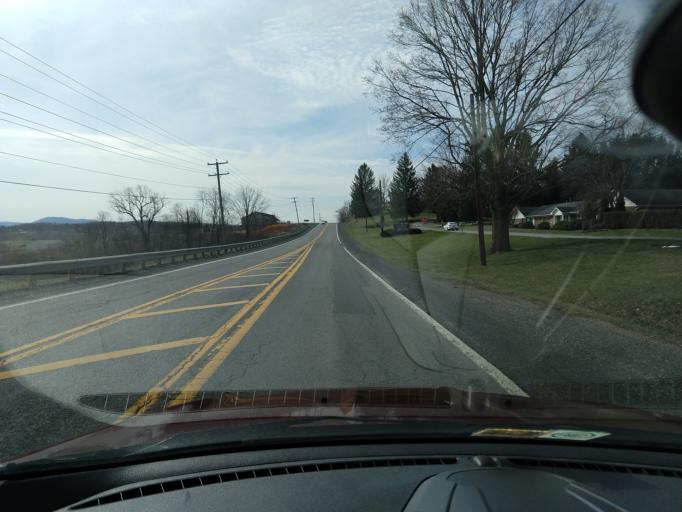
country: US
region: West Virginia
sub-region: Greenbrier County
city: Lewisburg
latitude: 37.8440
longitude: -80.4148
